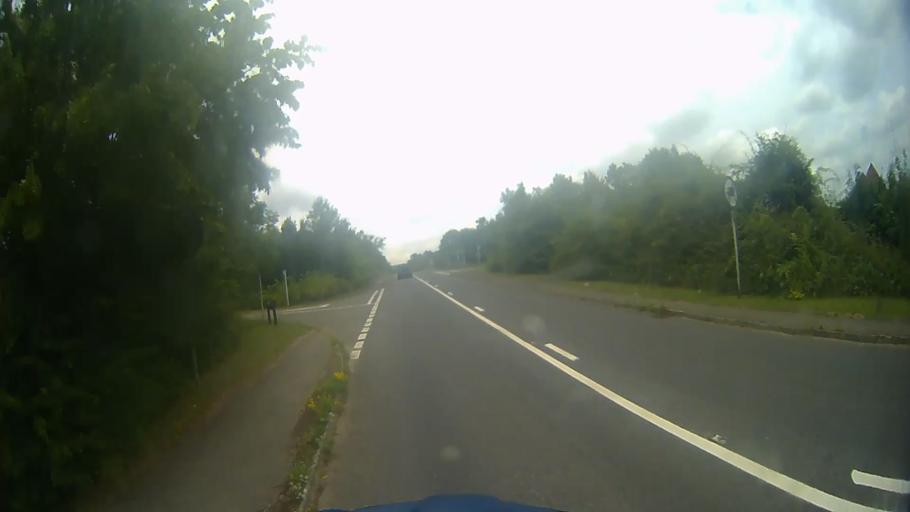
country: GB
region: England
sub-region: Hampshire
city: Kingsley
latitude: 51.1858
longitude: -0.8783
